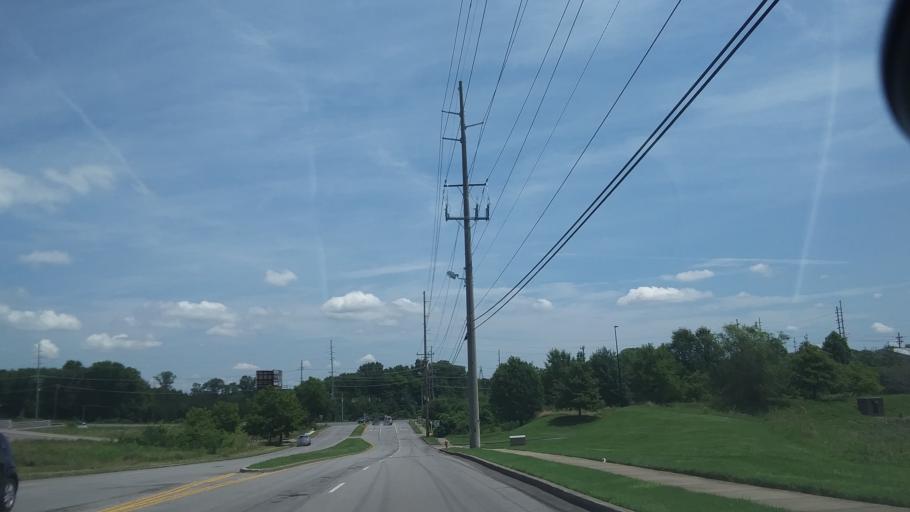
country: US
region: Tennessee
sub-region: Rutherford County
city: La Vergne
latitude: 36.0631
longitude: -86.6302
